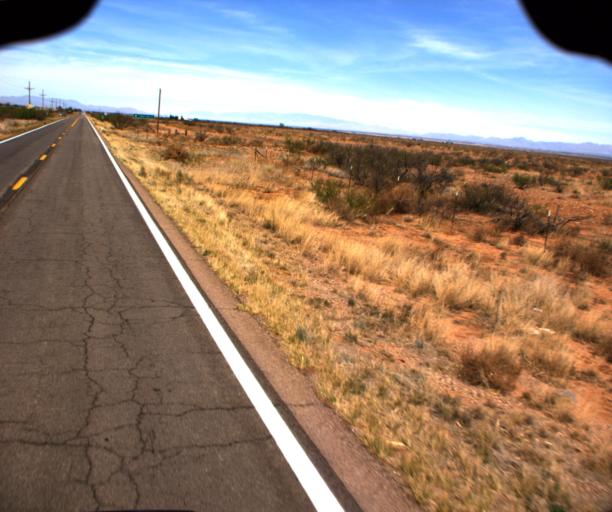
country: US
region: Arizona
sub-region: Cochise County
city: Tombstone
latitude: 31.9190
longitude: -109.8203
